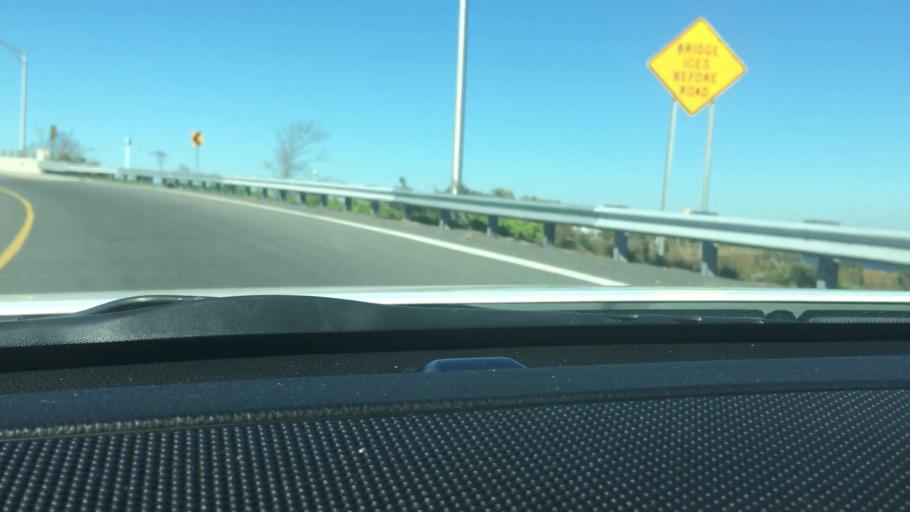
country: US
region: New Jersey
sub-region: Atlantic County
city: Pleasantville
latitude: 39.3957
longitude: -74.4917
